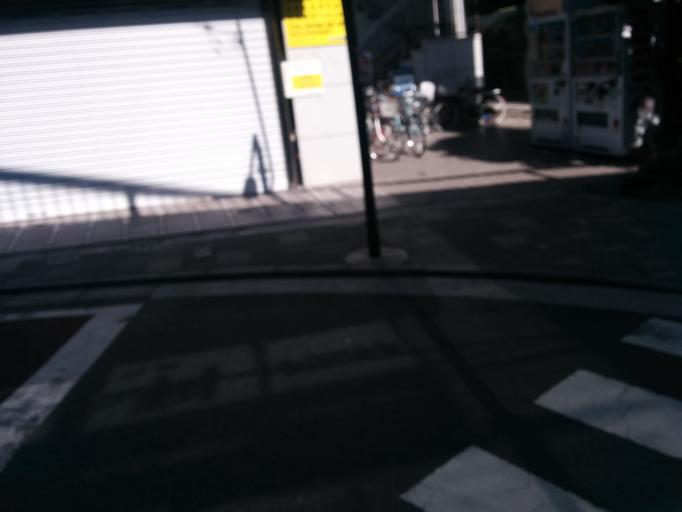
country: JP
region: Tokyo
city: Tokyo
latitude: 35.7259
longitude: 139.6951
